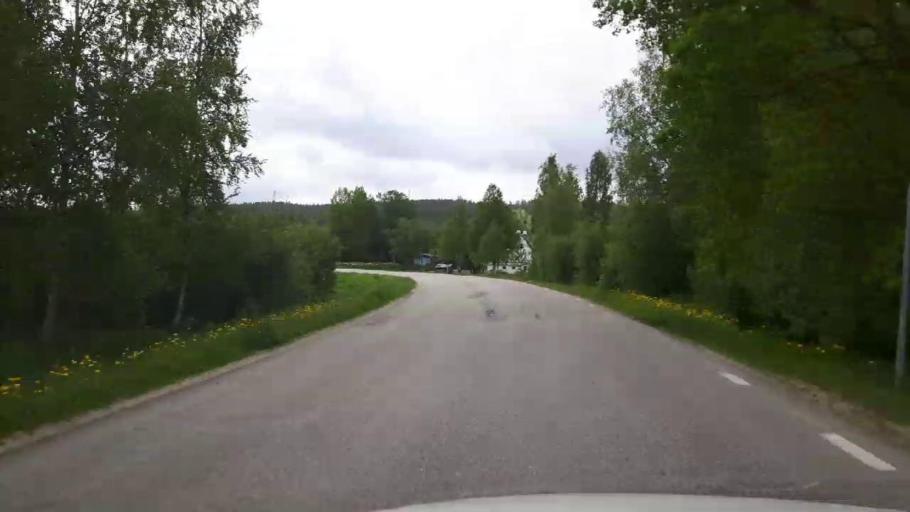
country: SE
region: Gaevleborg
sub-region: Ovanakers Kommun
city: Edsbyn
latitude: 61.3618
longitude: 15.8949
